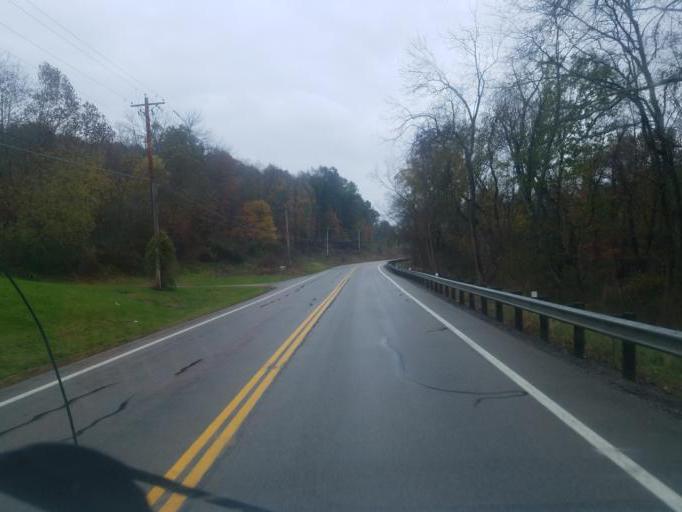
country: US
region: Ohio
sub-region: Muskingum County
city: Frazeysburg
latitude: 40.0473
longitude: -82.1255
